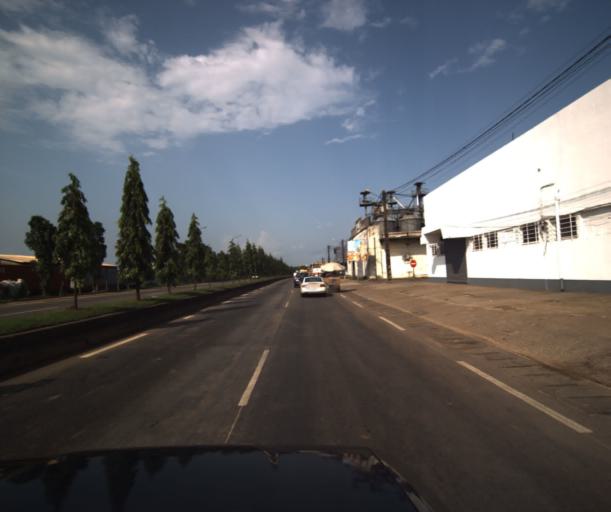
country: CM
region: Littoral
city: Douala
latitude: 4.0578
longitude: 9.6973
